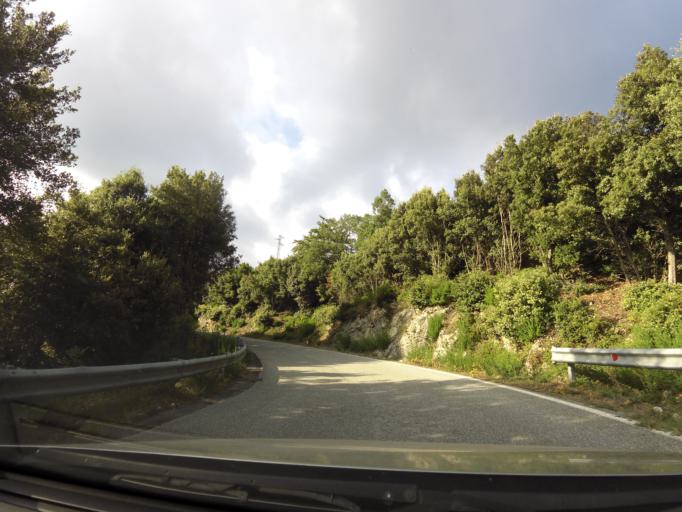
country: IT
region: Calabria
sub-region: Provincia di Vibo-Valentia
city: Nardodipace
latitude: 38.4786
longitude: 16.3828
